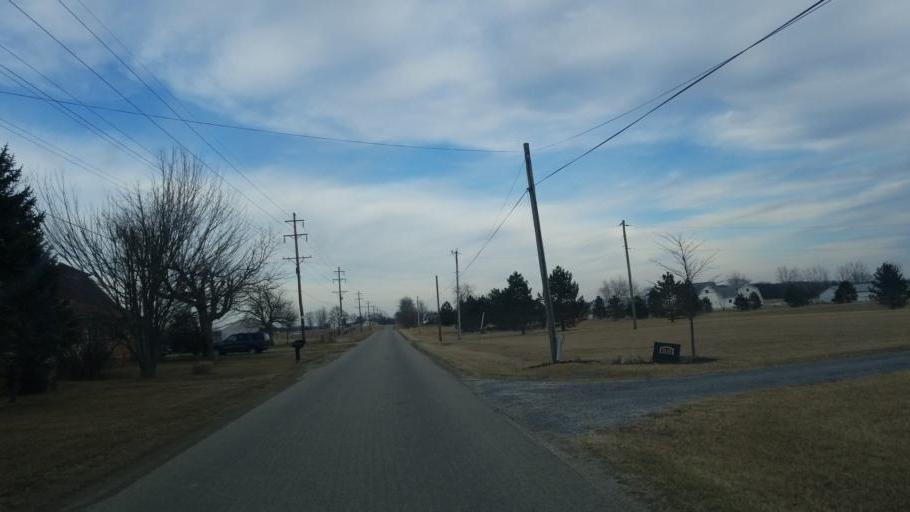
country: US
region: Ohio
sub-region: Defiance County
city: Hicksville
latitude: 41.3537
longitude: -84.7457
